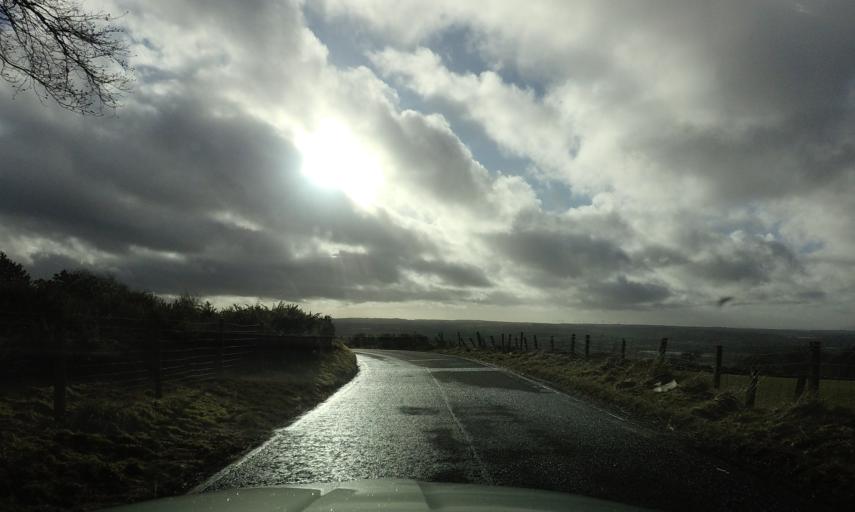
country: GB
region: Scotland
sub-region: West Lothian
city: Bathgate
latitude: 55.9263
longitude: -3.6335
